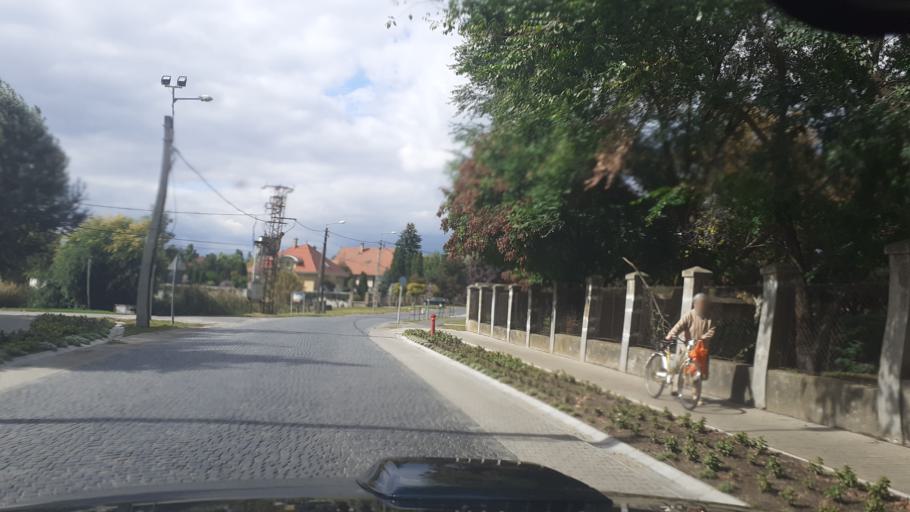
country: HU
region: Bacs-Kiskun
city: Solt
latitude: 46.8029
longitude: 18.9989
